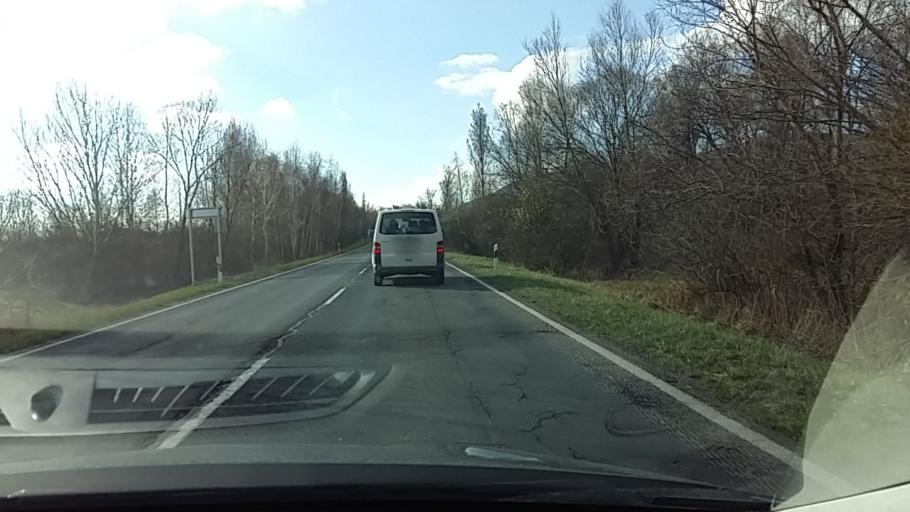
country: HU
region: Veszprem
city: Tapolca
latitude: 46.8430
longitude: 17.3711
